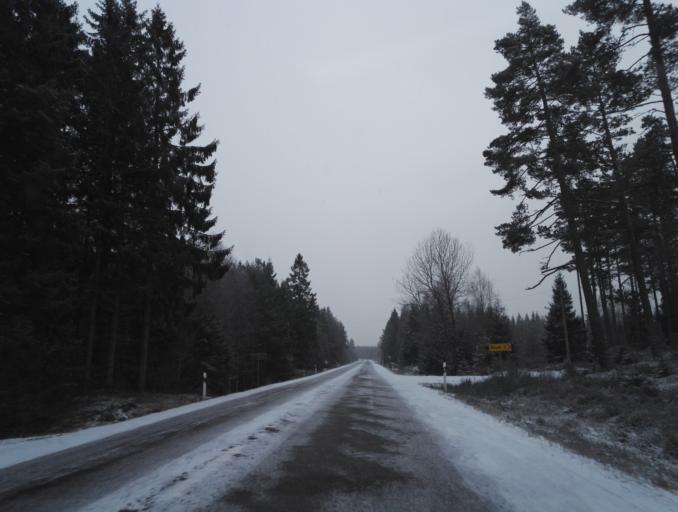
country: SE
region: Kronoberg
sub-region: Uppvidinge Kommun
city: Lenhovda
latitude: 56.8859
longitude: 15.3752
